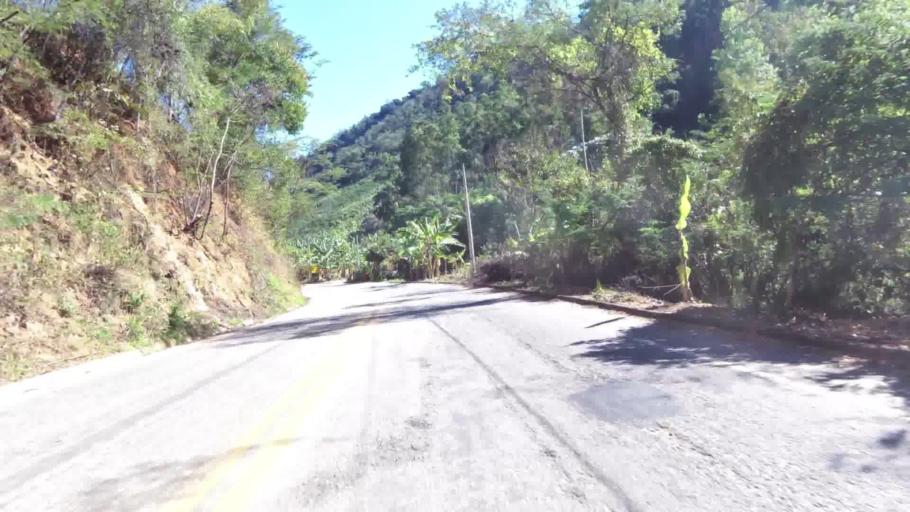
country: BR
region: Espirito Santo
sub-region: Iconha
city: Iconha
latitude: -20.7402
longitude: -40.8678
